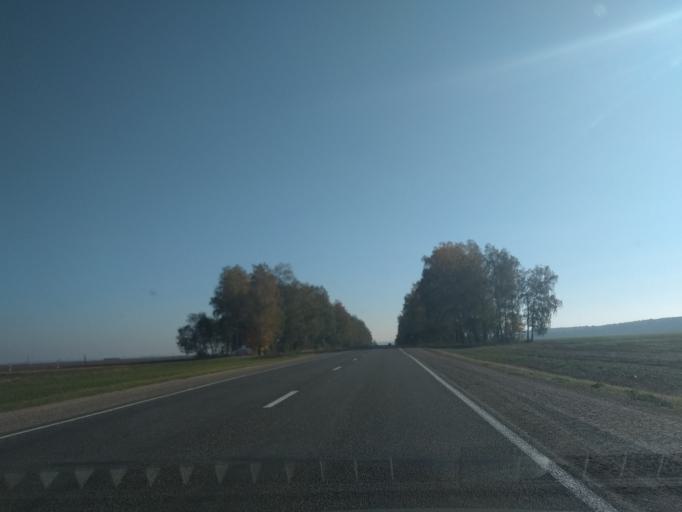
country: BY
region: Grodnenskaya
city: Slonim
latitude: 53.1223
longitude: 25.0902
